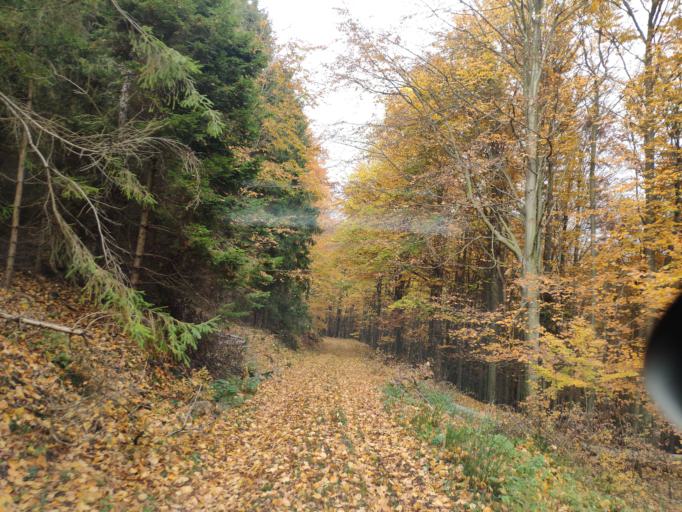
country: SK
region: Kosicky
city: Medzev
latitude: 48.7530
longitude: 20.9843
